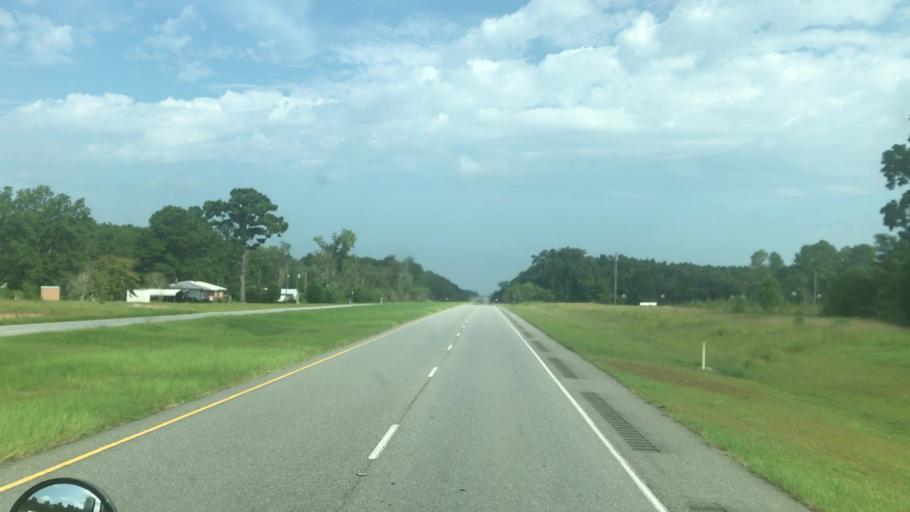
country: US
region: Georgia
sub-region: Early County
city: Blakely
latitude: 31.2923
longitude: -84.8506
